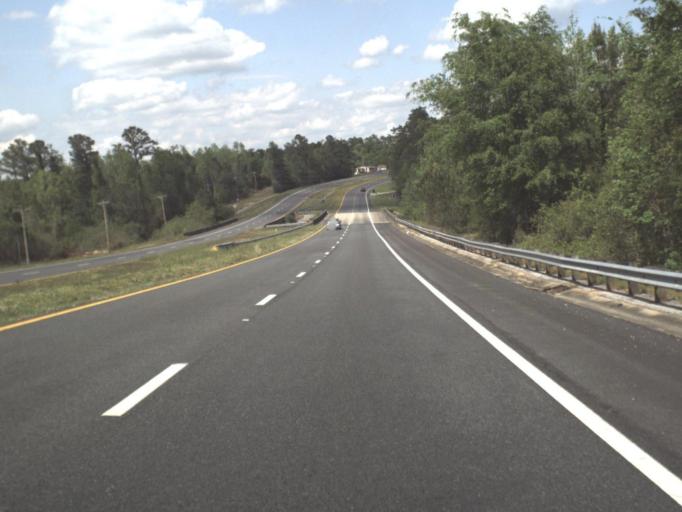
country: US
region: Florida
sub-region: Escambia County
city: Century
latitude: 30.9179
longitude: -87.3145
